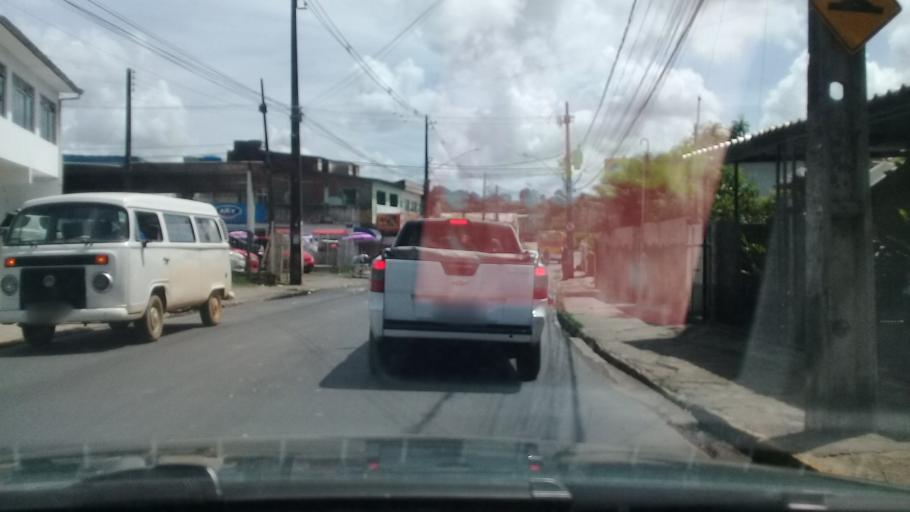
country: BR
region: Pernambuco
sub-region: Jaboatao Dos Guararapes
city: Jaboatao dos Guararapes
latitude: -8.0935
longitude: -35.0228
